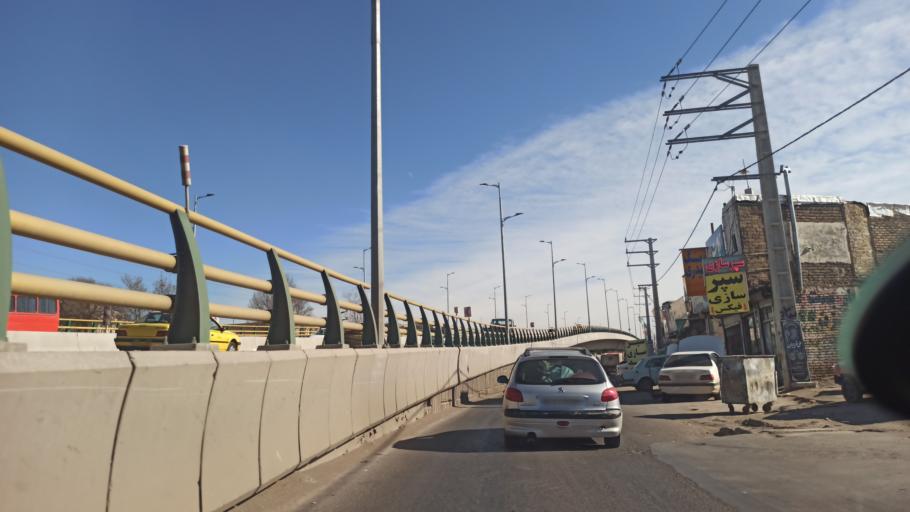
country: IR
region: Qazvin
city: Qazvin
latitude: 36.2579
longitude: 49.9925
